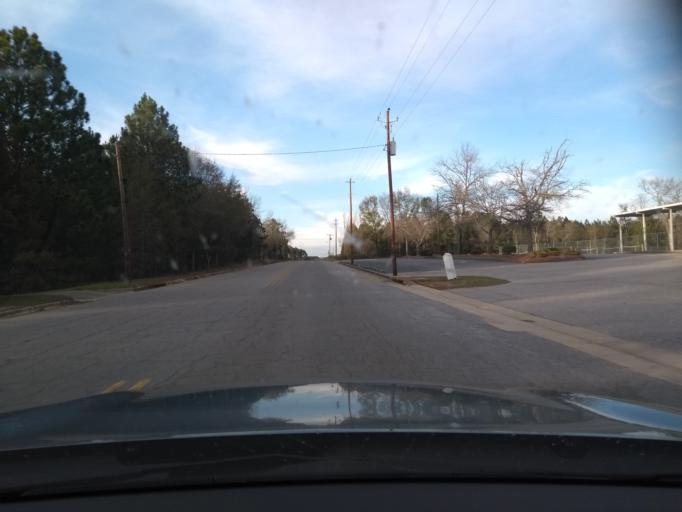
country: US
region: Georgia
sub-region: Bulloch County
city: Brooklet
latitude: 32.2689
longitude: -81.7602
